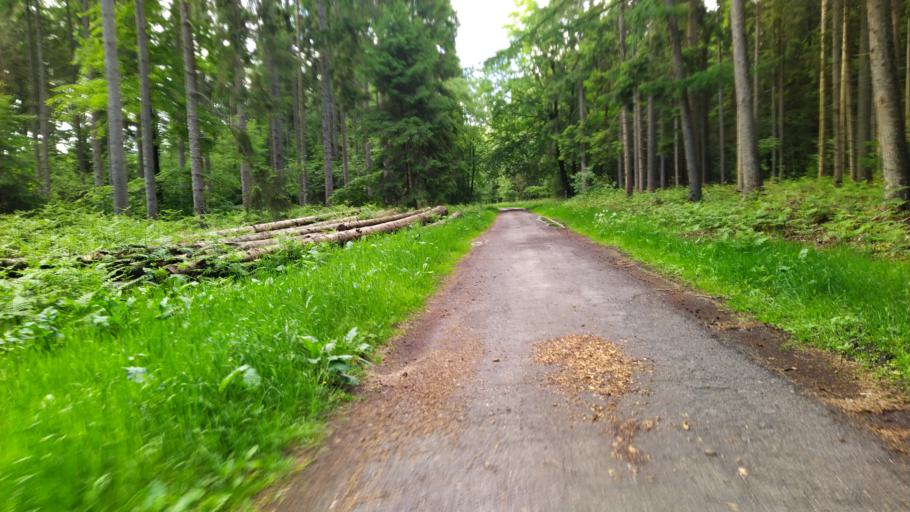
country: DE
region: Lower Saxony
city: Farven
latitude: 53.4407
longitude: 9.2862
